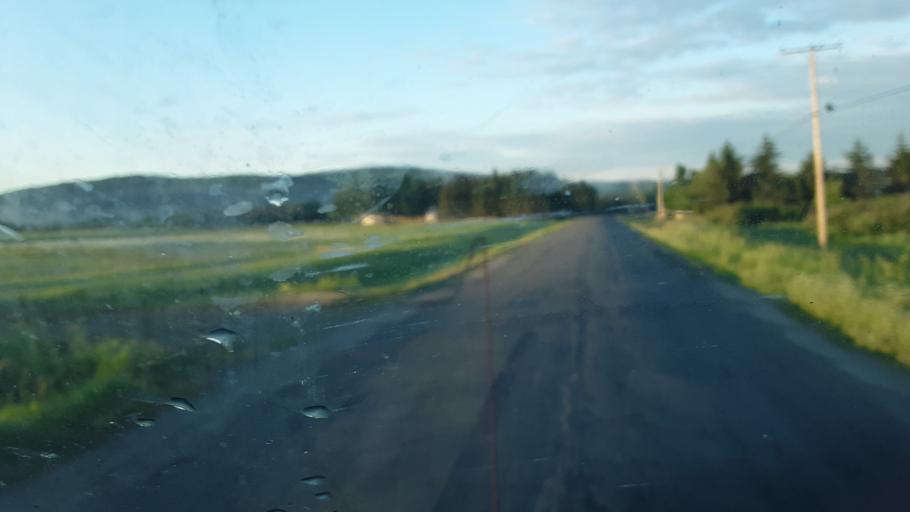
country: US
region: Maine
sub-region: Aroostook County
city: Presque Isle
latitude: 46.7607
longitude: -68.1020
